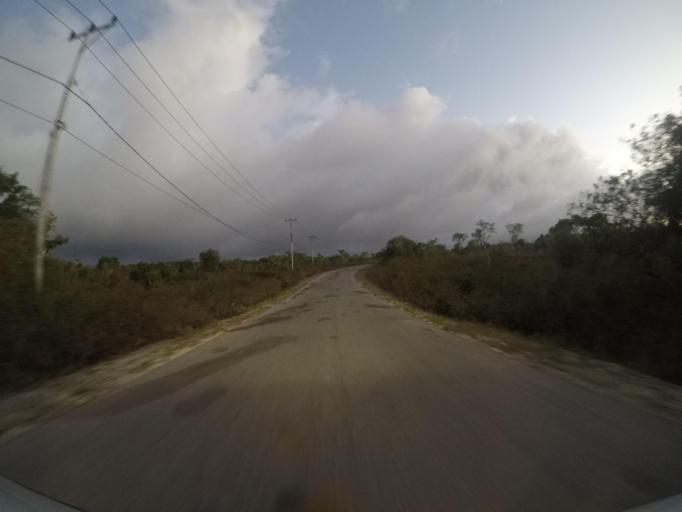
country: TL
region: Lautem
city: Lospalos
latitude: -8.3707
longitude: 127.0211
